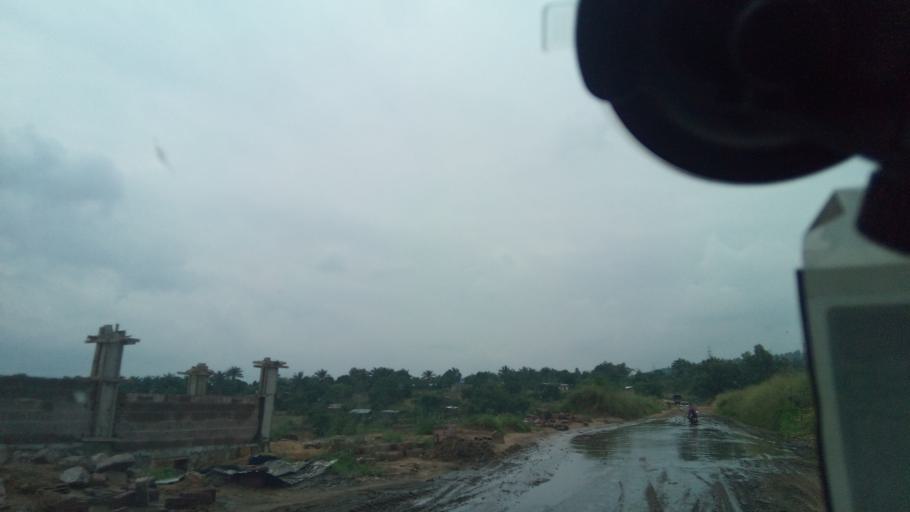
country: CG
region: Brazzaville
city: Brazzaville
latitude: -4.0773
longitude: 15.5432
